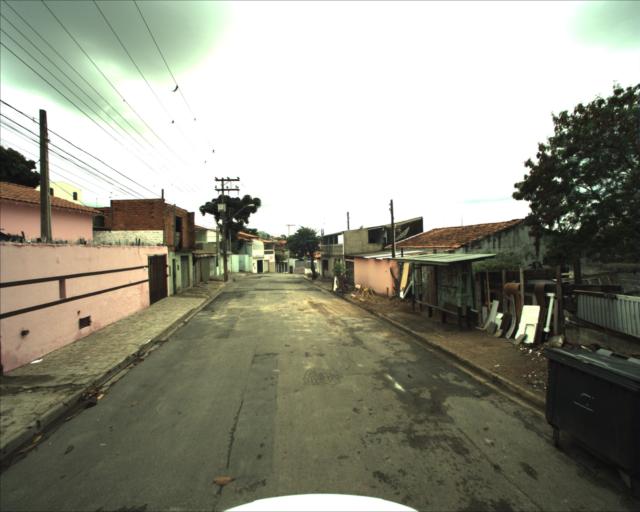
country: BR
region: Sao Paulo
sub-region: Sorocaba
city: Sorocaba
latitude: -23.5037
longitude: -47.5053
